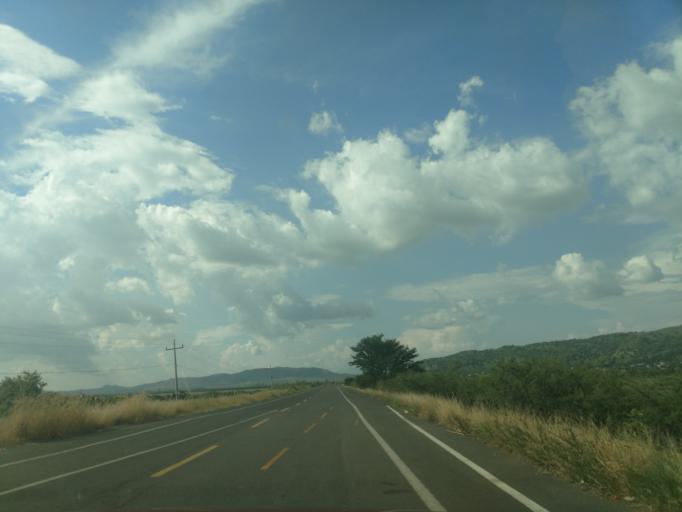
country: MX
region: Jalisco
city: Antonio Escobedo
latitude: 20.8977
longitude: -103.9945
